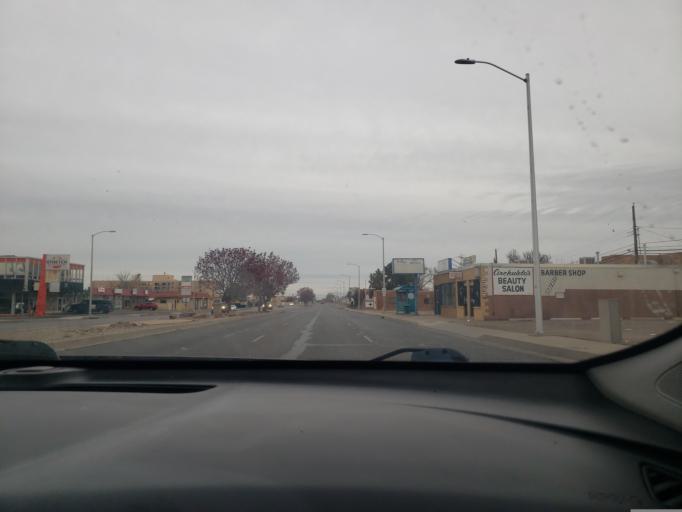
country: US
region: New Mexico
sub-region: Bernalillo County
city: Albuquerque
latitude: 35.0821
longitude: -106.5861
